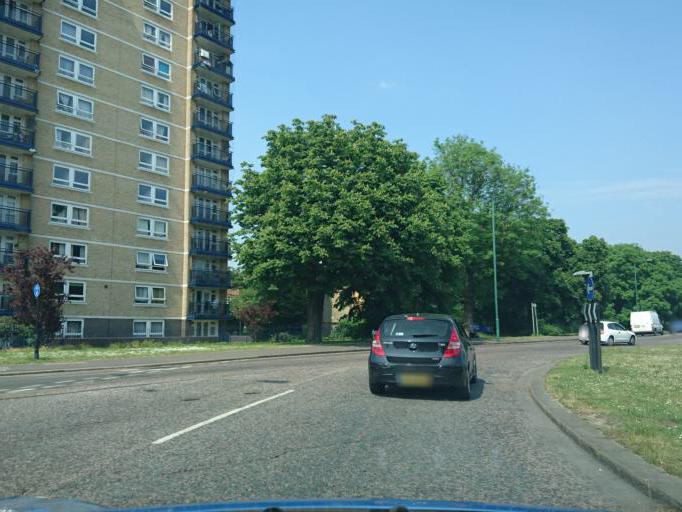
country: GB
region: England
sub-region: Greater London
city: Walthamstow
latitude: 51.5815
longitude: 0.0012
